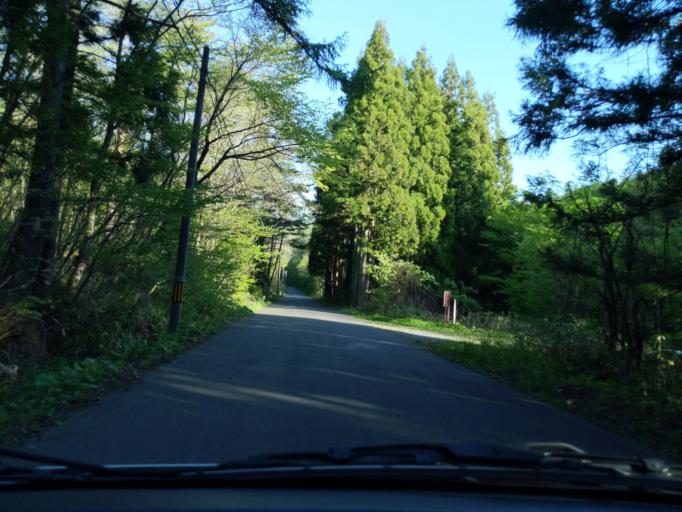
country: JP
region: Iwate
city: Ichinoseki
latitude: 38.8763
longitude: 140.9192
